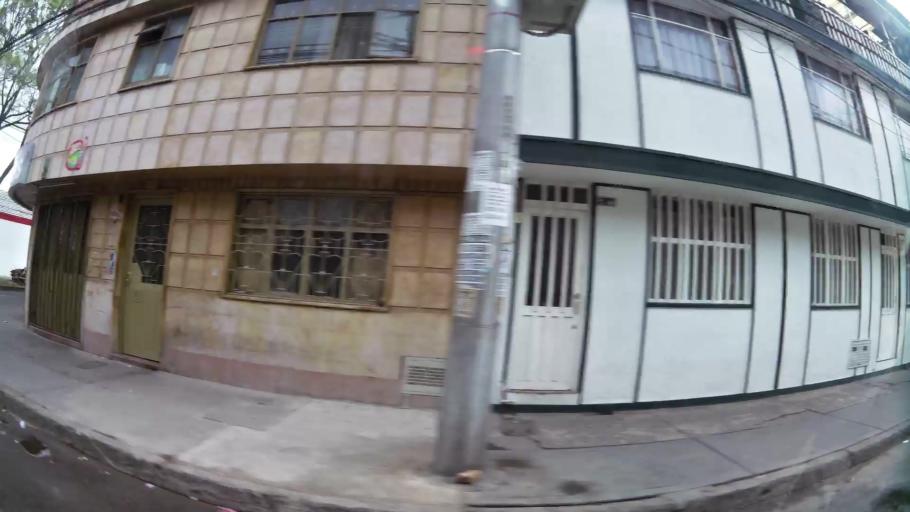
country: CO
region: Bogota D.C.
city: Bogota
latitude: 4.6266
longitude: -74.1209
